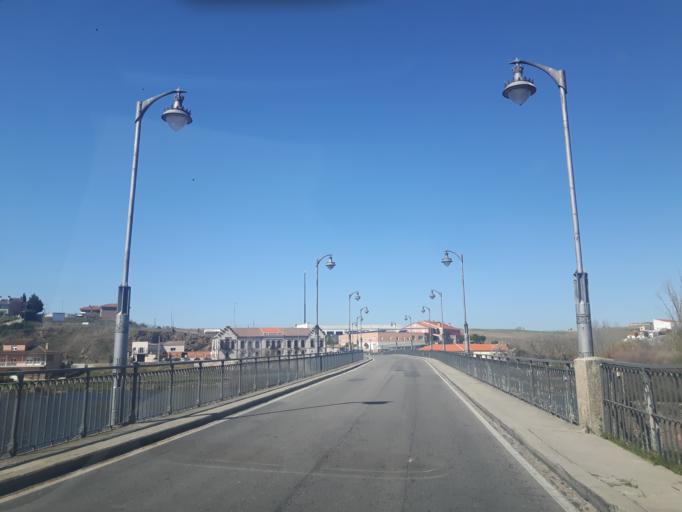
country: ES
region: Castille and Leon
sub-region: Provincia de Salamanca
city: Alba de Tormes
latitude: 40.8256
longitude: -5.5176
